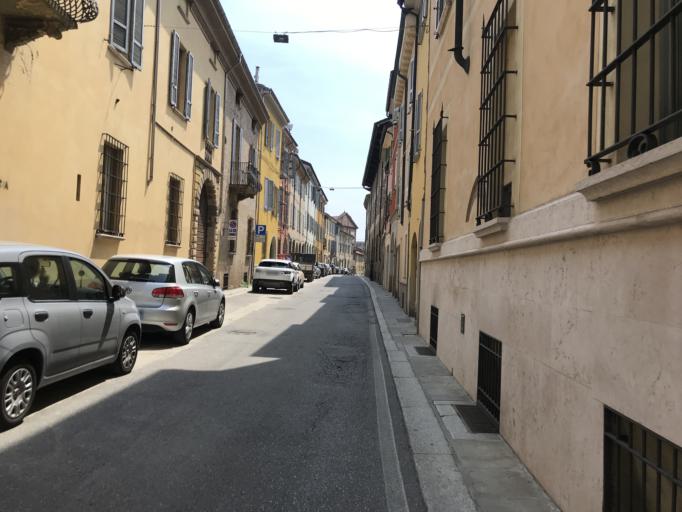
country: IT
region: Emilia-Romagna
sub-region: Provincia di Piacenza
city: Piacenza
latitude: 45.0498
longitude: 9.6993
